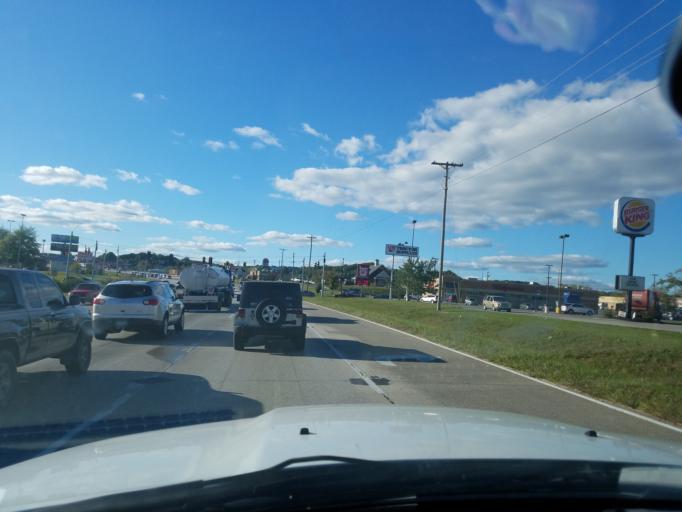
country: US
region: Kentucky
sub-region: Laurel County
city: London
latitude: 37.1101
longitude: -84.0908
